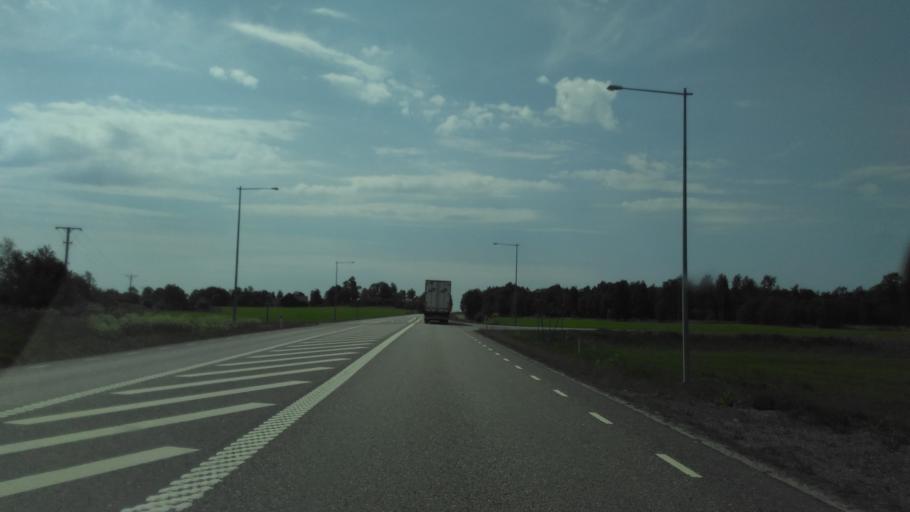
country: SE
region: Vaestra Goetaland
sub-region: Grastorps Kommun
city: Graestorp
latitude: 58.4041
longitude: 12.8223
